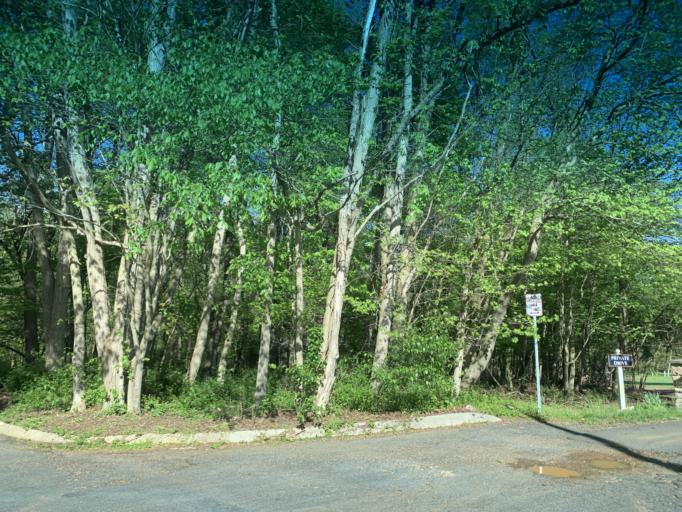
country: US
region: Maryland
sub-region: Harford County
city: Aberdeen
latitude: 39.5414
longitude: -76.2038
